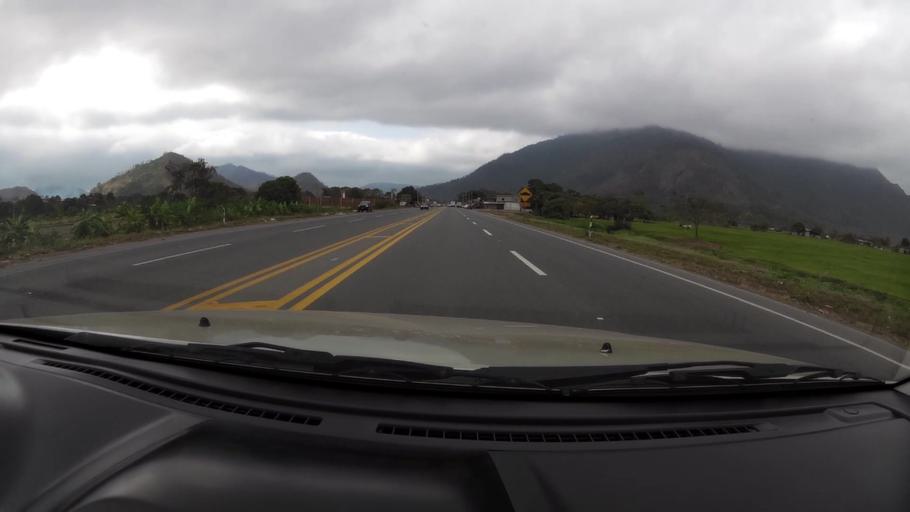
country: EC
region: Guayas
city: Coronel Marcelino Mariduena
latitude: -2.3815
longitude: -79.6313
